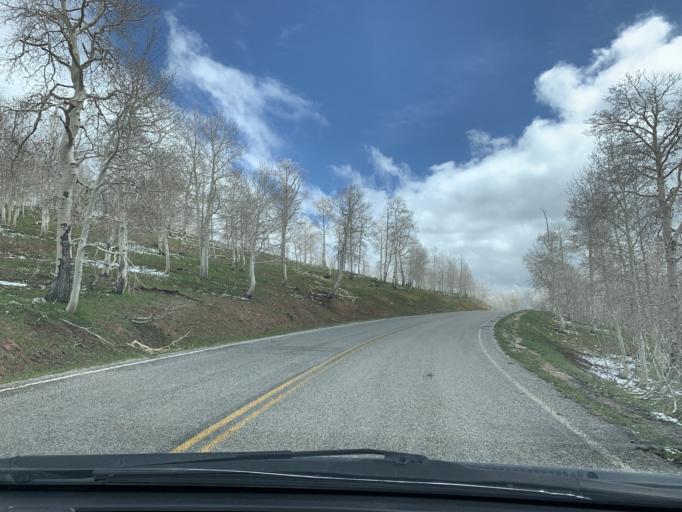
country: US
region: Utah
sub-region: Juab County
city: Mona
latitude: 39.8452
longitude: -111.7180
